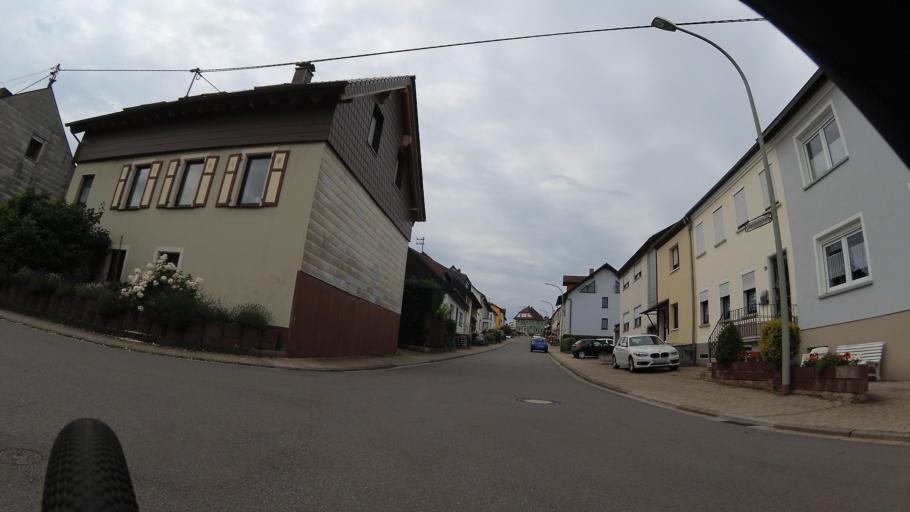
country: DE
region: Saarland
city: Quierschied
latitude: 49.3206
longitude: 7.0486
